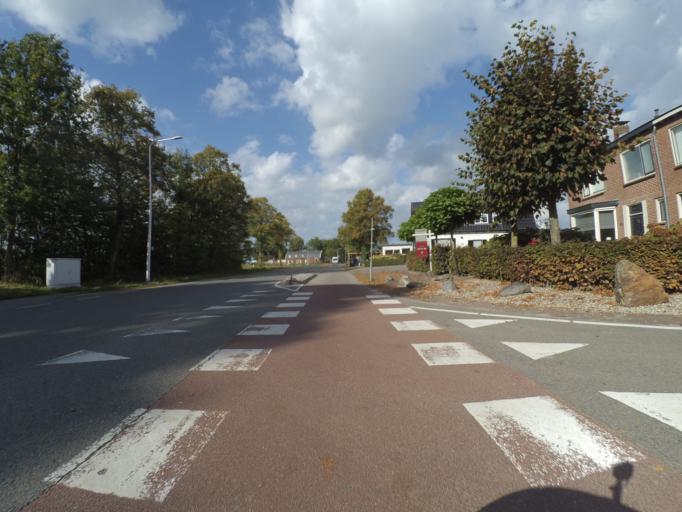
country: NL
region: Gelderland
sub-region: Gemeente Ede
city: Ederveen
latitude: 52.0509
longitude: 5.5754
